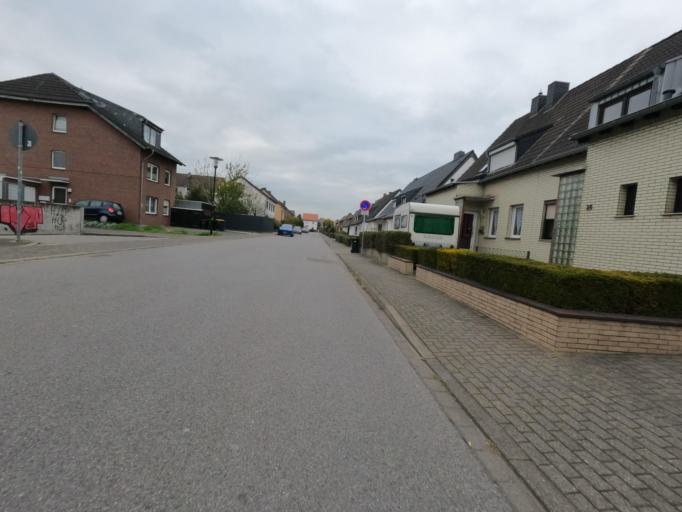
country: DE
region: North Rhine-Westphalia
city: Geilenkirchen
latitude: 50.9686
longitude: 6.1117
